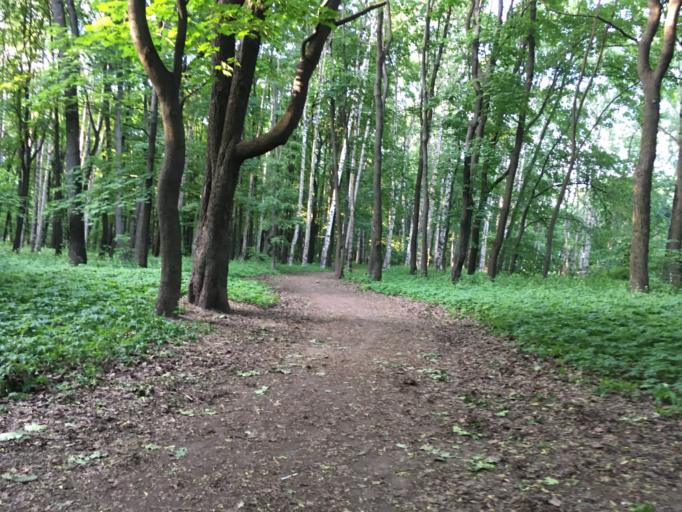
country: RU
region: Leningrad
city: Sampsonievskiy
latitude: 59.9908
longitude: 30.3470
